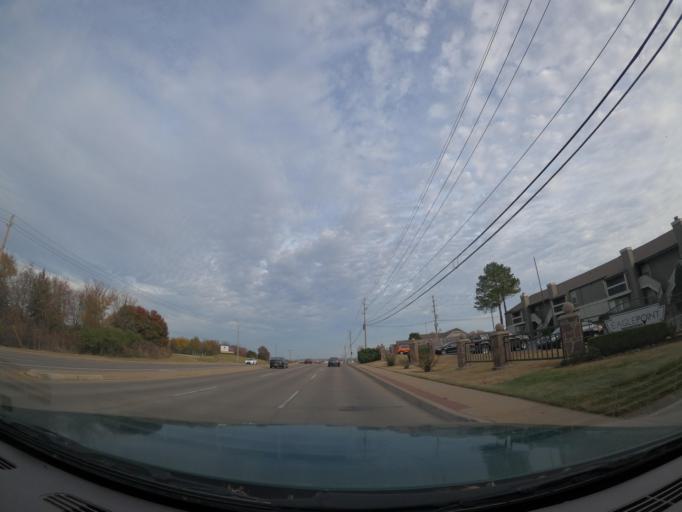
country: US
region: Oklahoma
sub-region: Tulsa County
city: Jenks
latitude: 36.0607
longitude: -95.9098
